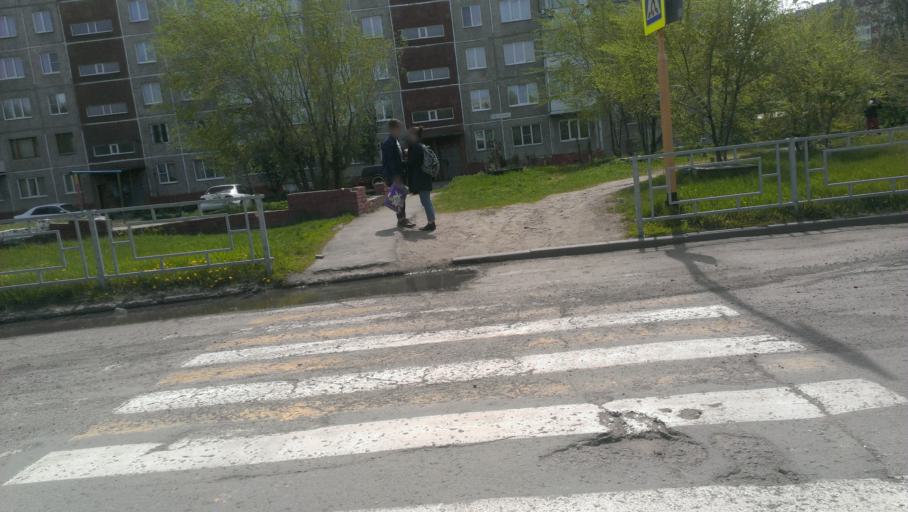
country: RU
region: Altai Krai
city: Novosilikatnyy
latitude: 53.3626
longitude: 83.6684
